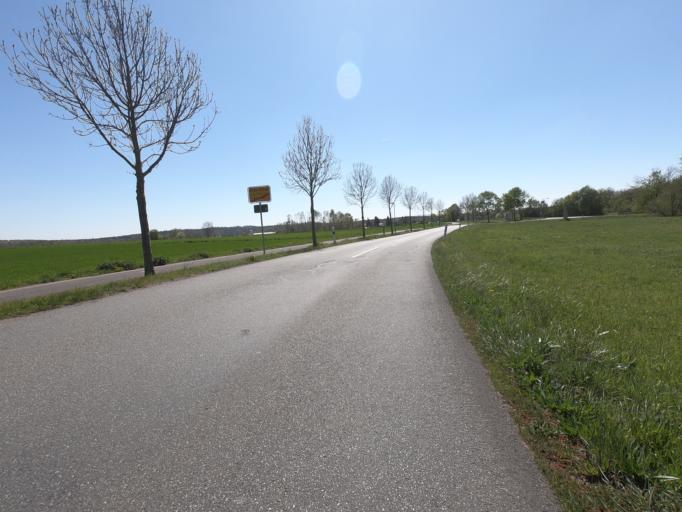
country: DE
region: Hesse
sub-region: Regierungsbezirk Darmstadt
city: Messel
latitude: 49.9295
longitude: 8.7421
